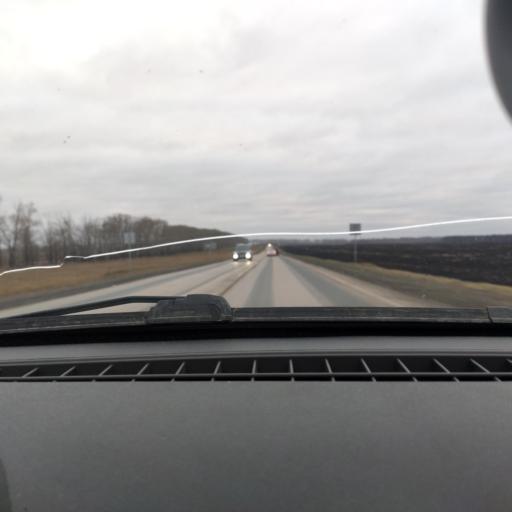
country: RU
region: Bashkortostan
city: Karmaskaly
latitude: 54.3851
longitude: 56.1731
